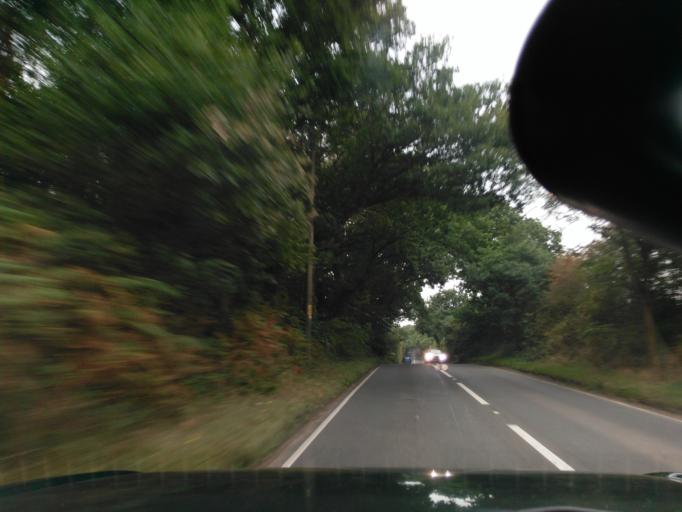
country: GB
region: England
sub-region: Dorset
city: Lytchett Matravers
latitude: 50.7465
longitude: -2.0383
